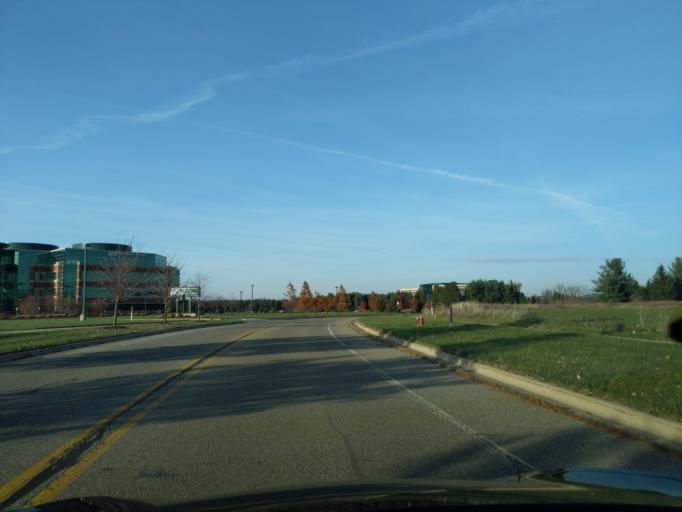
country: US
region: Michigan
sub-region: Ingham County
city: East Lansing
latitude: 42.7770
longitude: -84.5101
